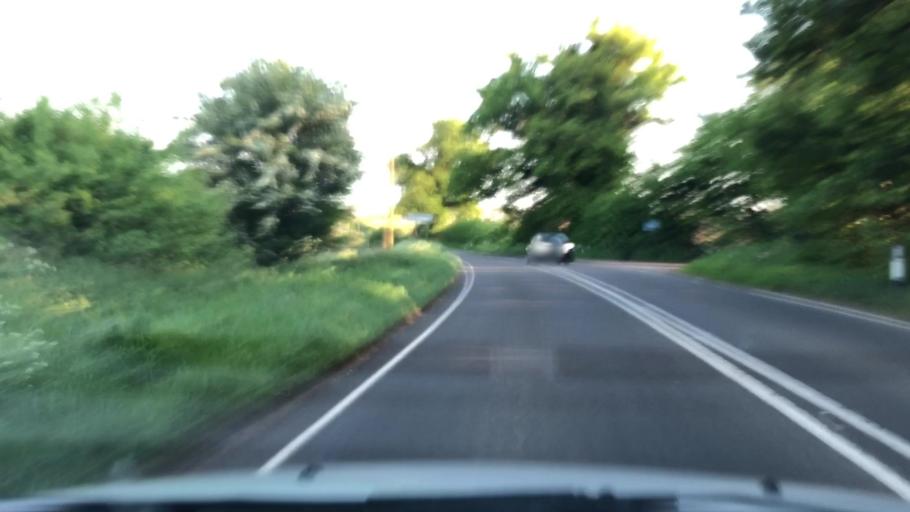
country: GB
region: England
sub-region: Hampshire
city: Alton
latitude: 51.1597
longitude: -0.9906
